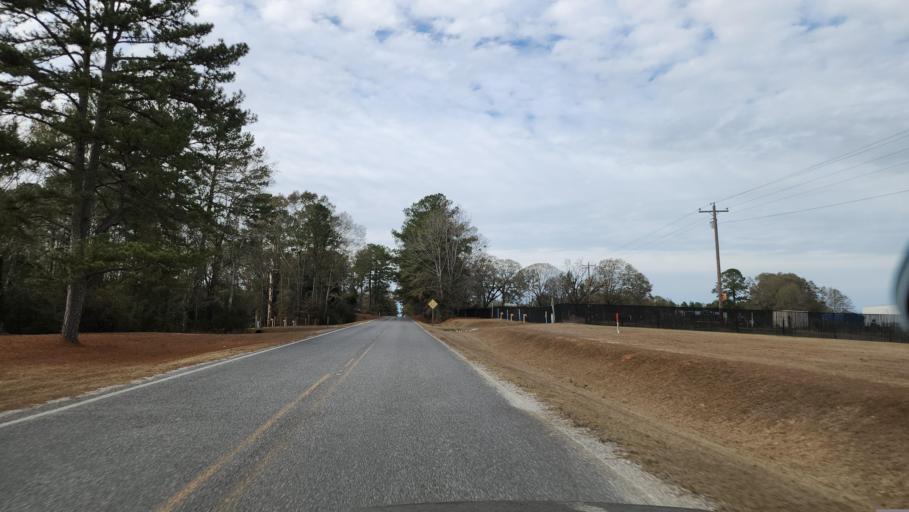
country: US
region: Mississippi
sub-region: Clarke County
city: Stonewall
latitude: 32.2019
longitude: -88.6867
